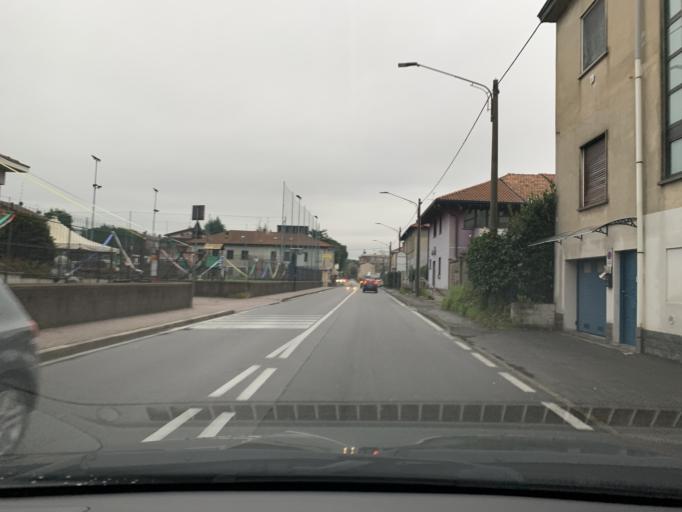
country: IT
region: Lombardy
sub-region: Provincia di Varese
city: Saronno
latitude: 45.6366
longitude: 9.0467
